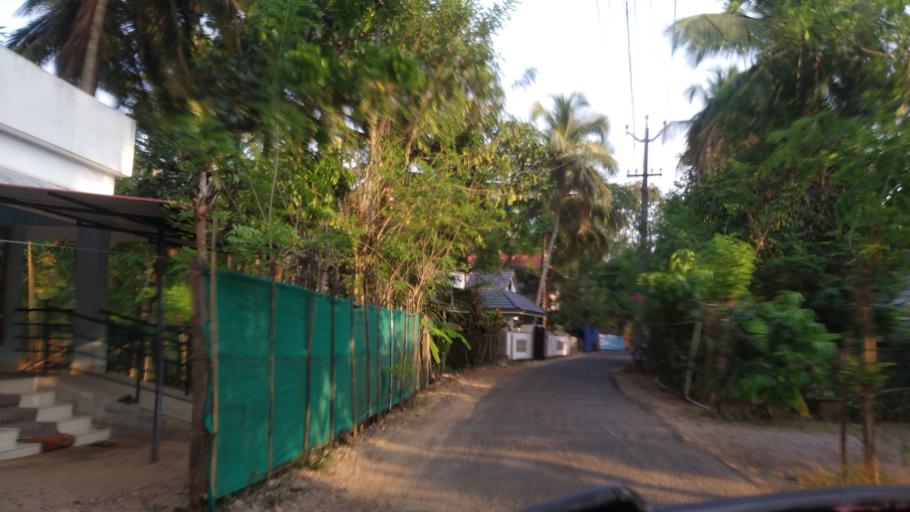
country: IN
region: Kerala
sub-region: Thrissur District
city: Thanniyam
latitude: 10.4194
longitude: 76.0852
